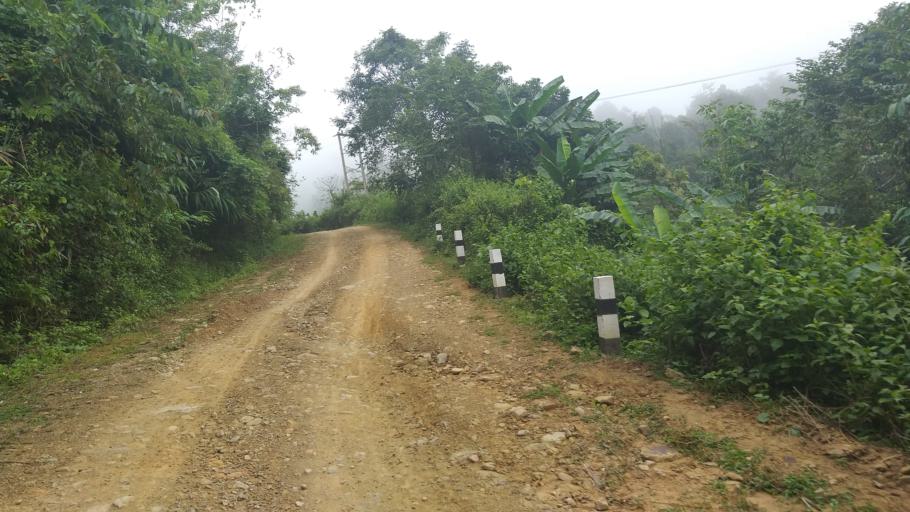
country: LA
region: Phongsali
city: Khoa
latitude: 21.2524
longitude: 102.6646
